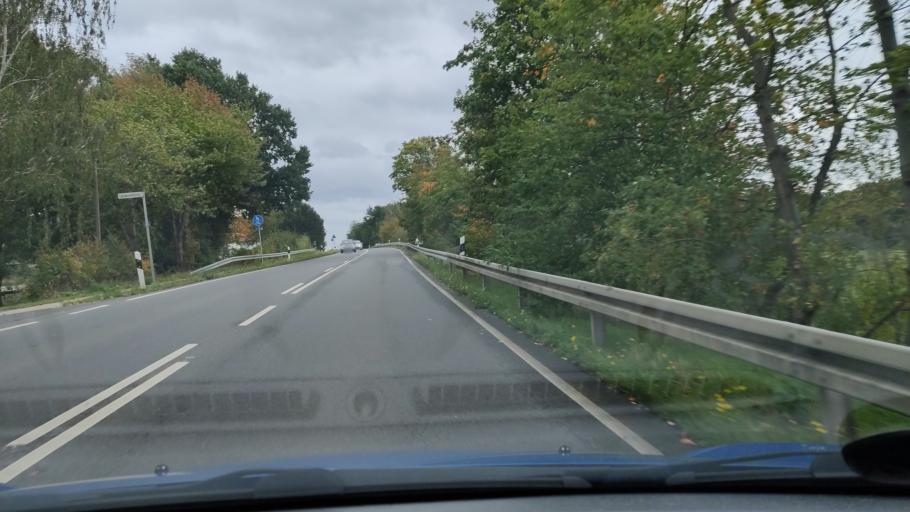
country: DE
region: Lower Saxony
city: Garbsen
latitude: 52.3986
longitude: 9.5468
